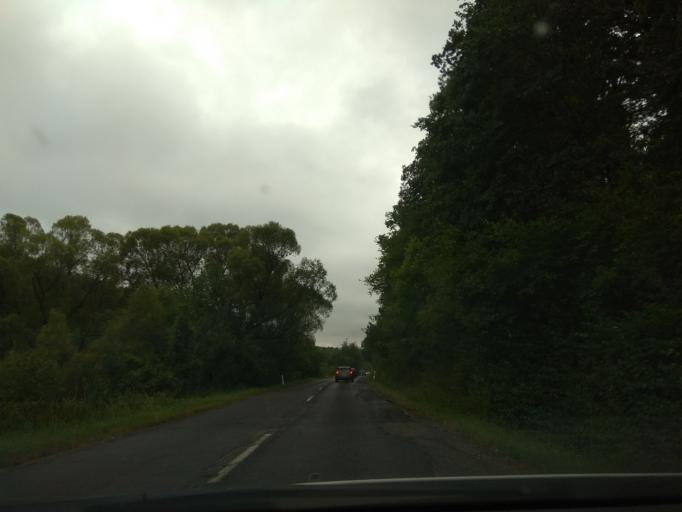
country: HU
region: Borsod-Abauj-Zemplen
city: Harsany
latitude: 48.0113
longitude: 20.7628
